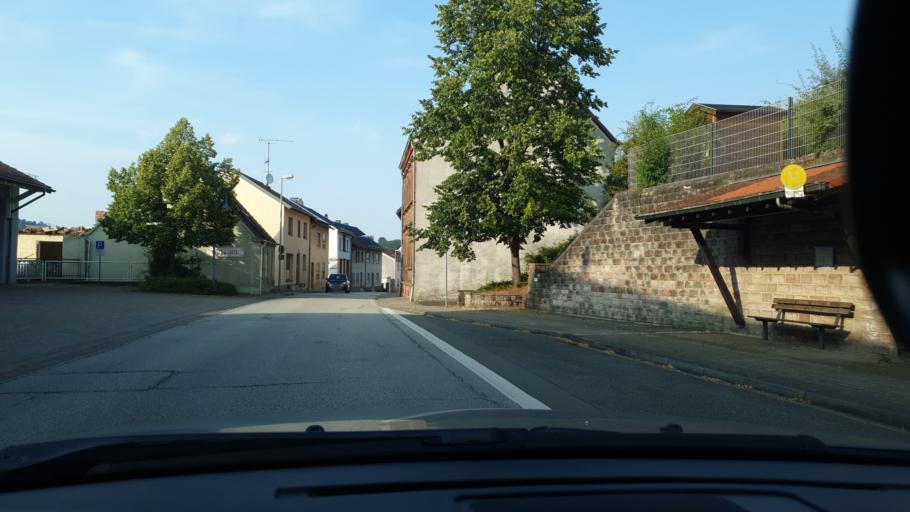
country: DE
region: Rheinland-Pfalz
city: Weilerbach
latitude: 49.4830
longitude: 7.6338
